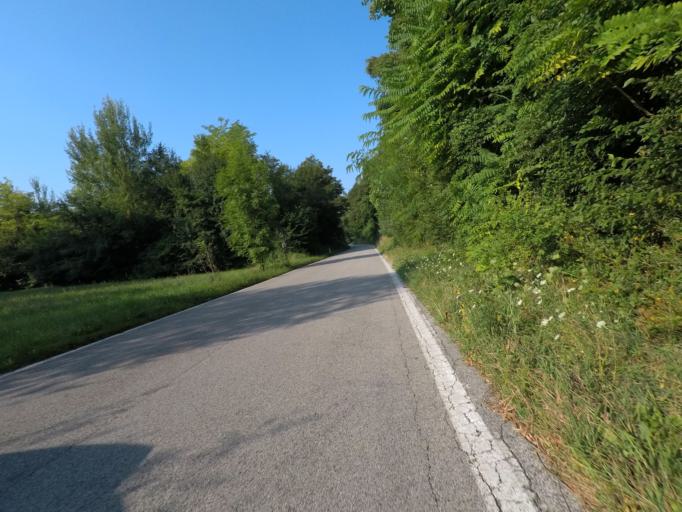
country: IT
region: Friuli Venezia Giulia
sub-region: Provincia di Udine
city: Forgaria nel Friuli
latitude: 46.2215
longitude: 13.0054
